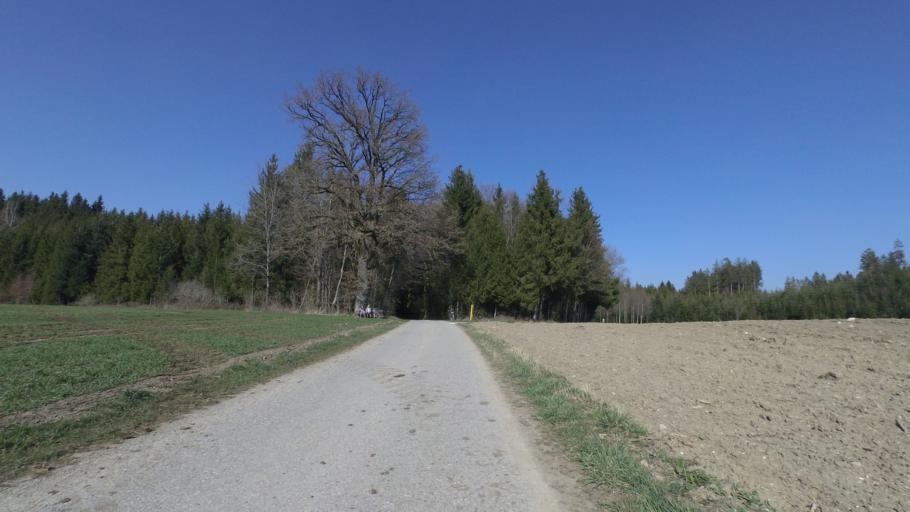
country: DE
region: Bavaria
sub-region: Upper Bavaria
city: Nussdorf
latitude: 47.9115
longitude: 12.5969
